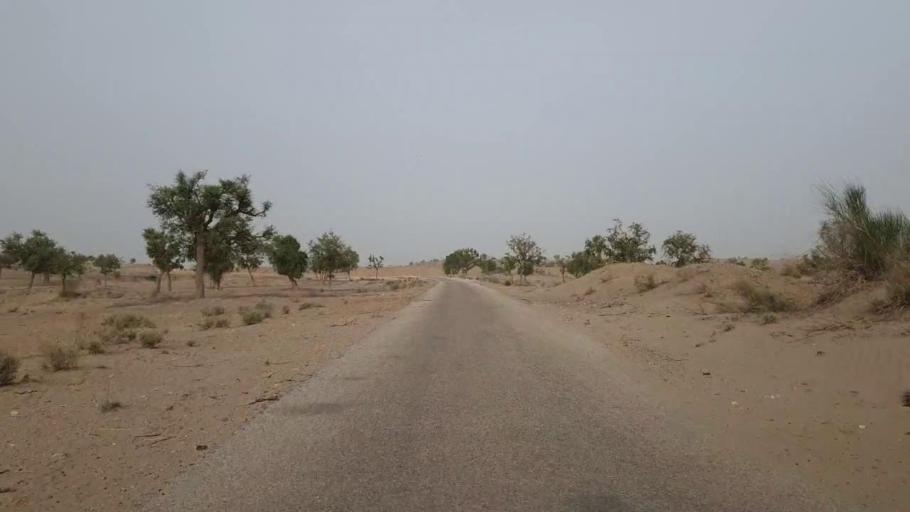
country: PK
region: Sindh
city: Islamkot
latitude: 24.5441
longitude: 70.3782
